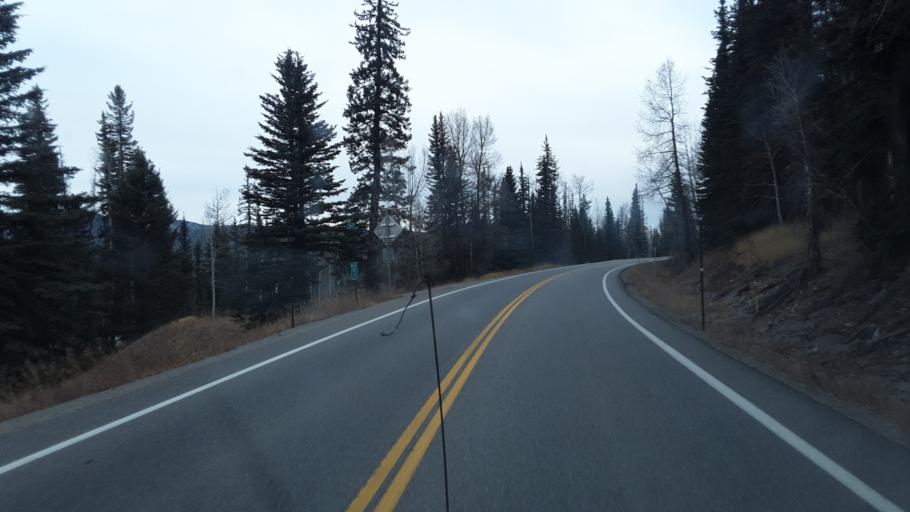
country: US
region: Colorado
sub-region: San Juan County
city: Silverton
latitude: 37.6577
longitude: -107.8113
